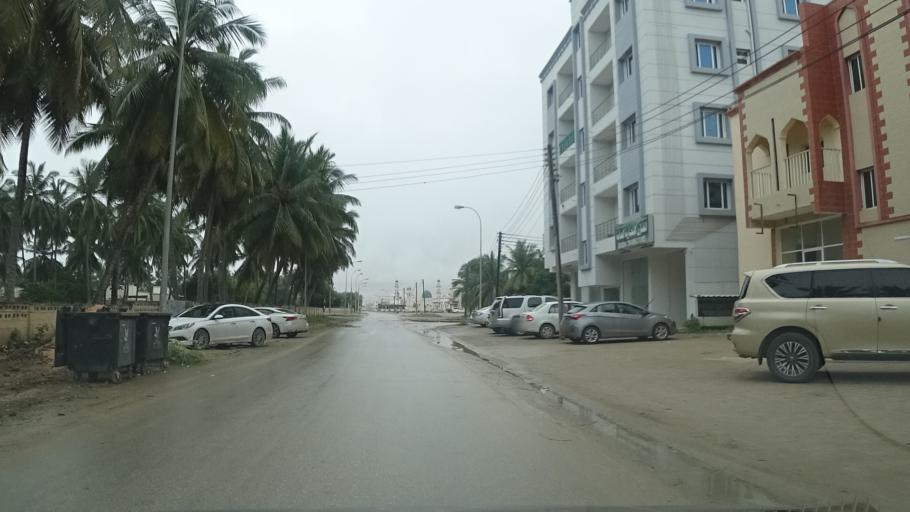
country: OM
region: Zufar
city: Salalah
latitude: 17.0015
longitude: 54.0469
